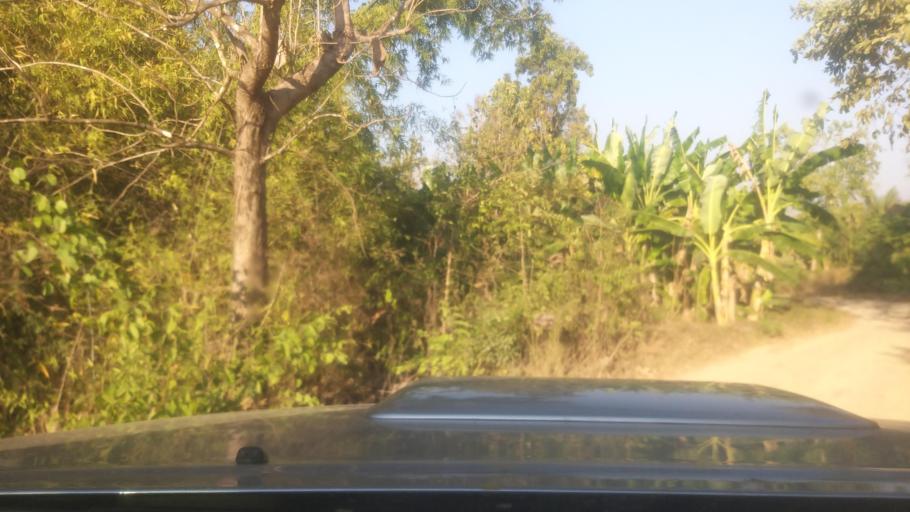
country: TH
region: Phrae
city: Phrae
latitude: 18.2639
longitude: 100.0180
